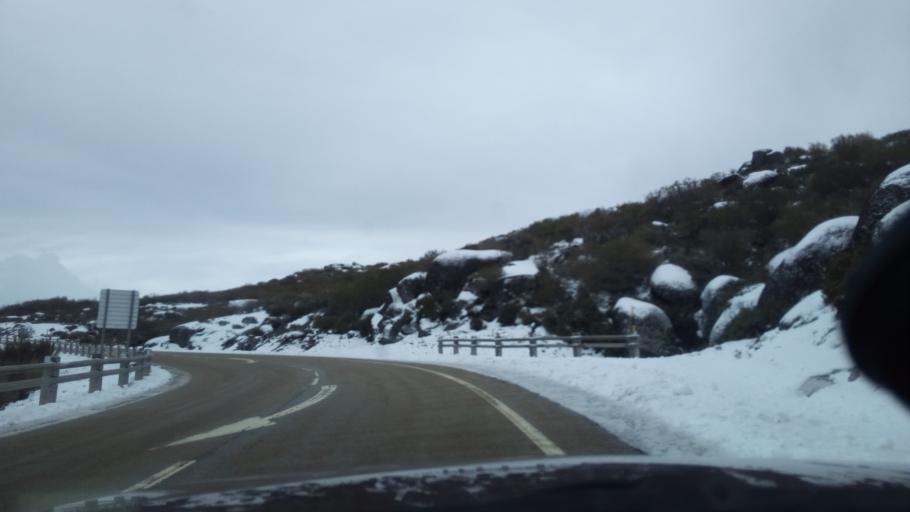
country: PT
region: Guarda
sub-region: Seia
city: Seia
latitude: 40.3551
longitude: -7.6653
